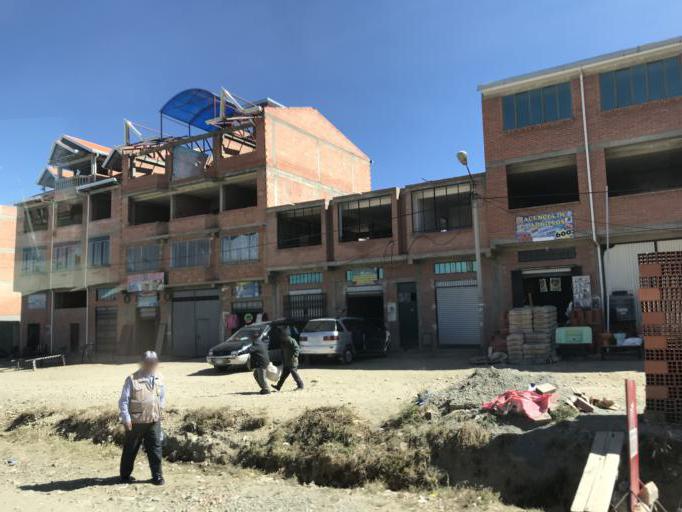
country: BO
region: La Paz
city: La Paz
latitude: -16.5033
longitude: -68.2466
